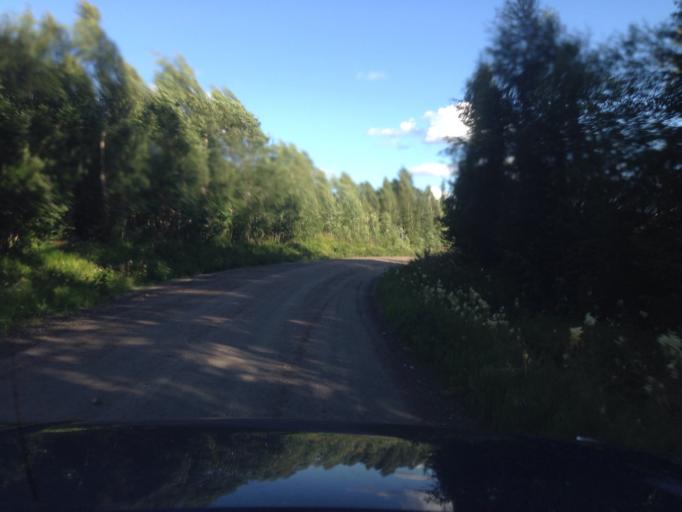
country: SE
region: Dalarna
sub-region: Ludvika Kommun
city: Abborrberget
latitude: 60.2296
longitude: 14.8394
